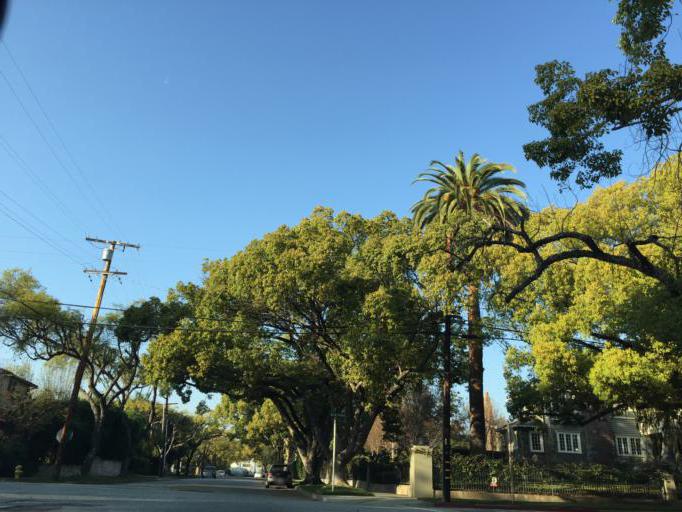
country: US
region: California
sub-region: Los Angeles County
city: South Pasadena
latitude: 34.1206
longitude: -118.1570
